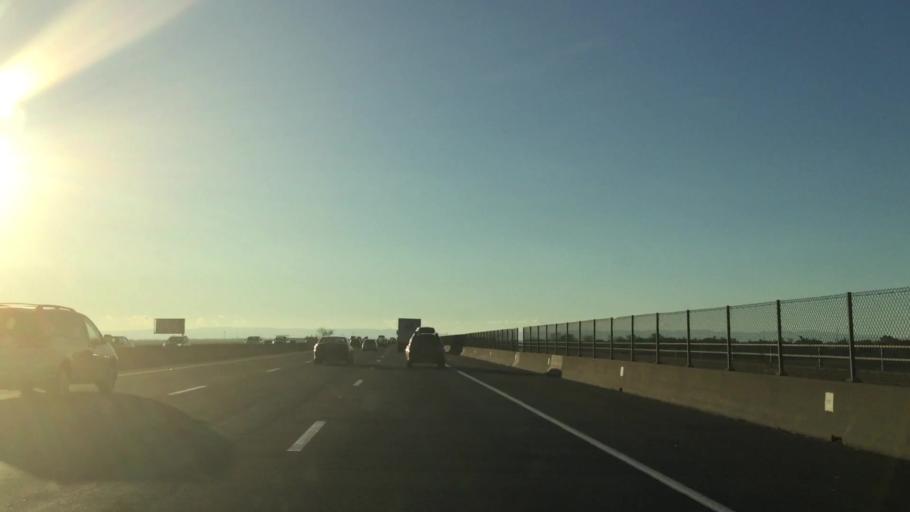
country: US
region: California
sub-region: Yolo County
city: West Sacramento
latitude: 38.5715
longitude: -121.5974
